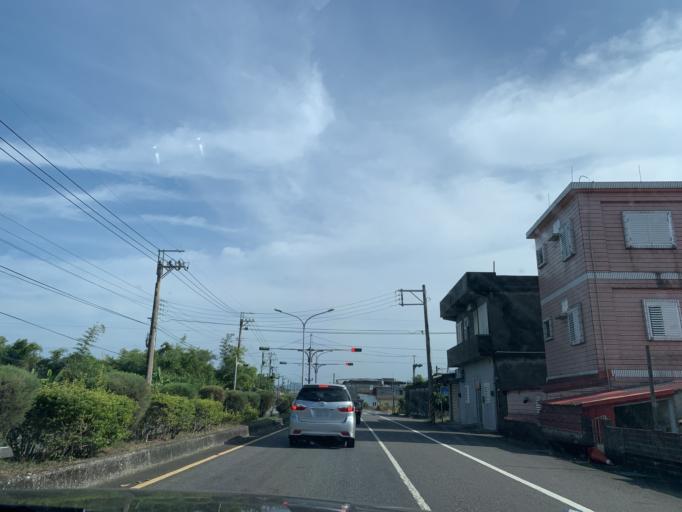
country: TW
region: Taiwan
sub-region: Yilan
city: Yilan
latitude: 24.7498
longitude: 121.8159
